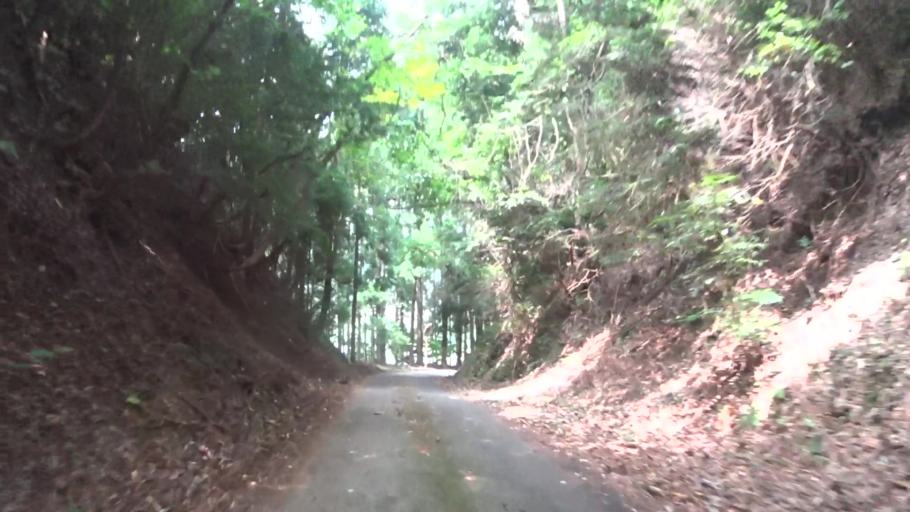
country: JP
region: Kyoto
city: Kameoka
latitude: 35.2041
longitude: 135.5841
